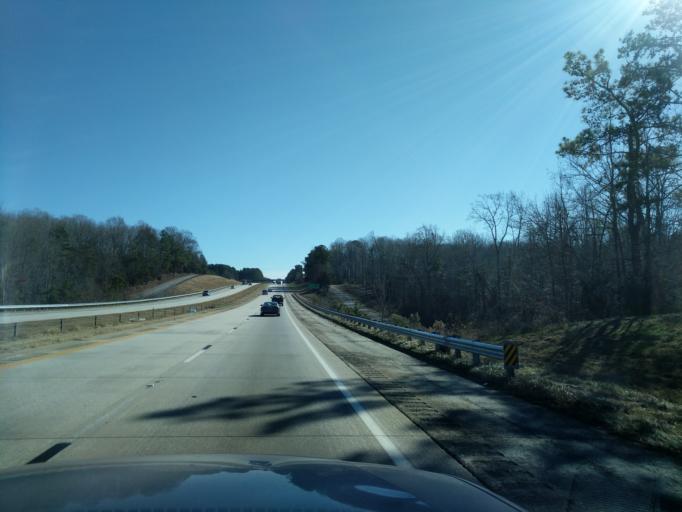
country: US
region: South Carolina
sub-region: Laurens County
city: Watts Mills
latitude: 34.5345
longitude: -81.9411
